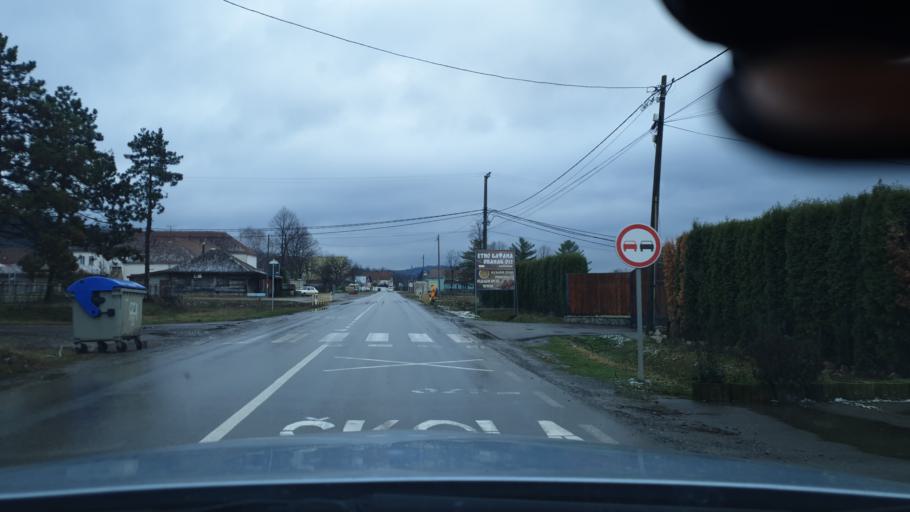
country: RS
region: Central Serbia
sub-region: Branicevski Okrug
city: Petrovac
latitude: 44.4048
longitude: 21.3961
